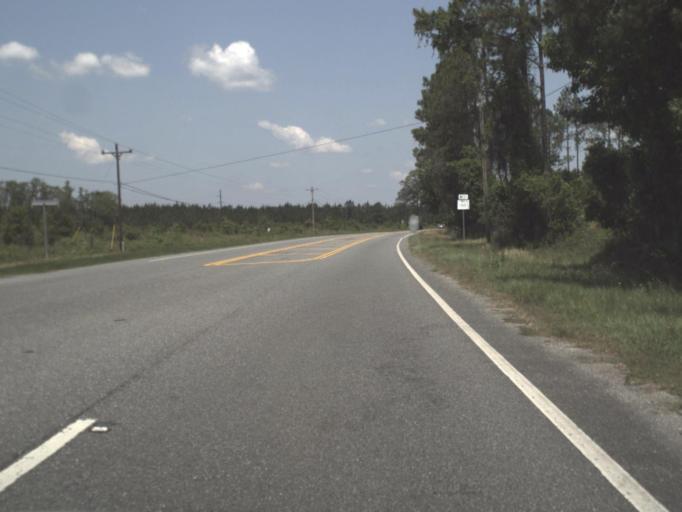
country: US
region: Florida
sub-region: Bradford County
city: Starke
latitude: 29.9456
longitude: -82.1372
